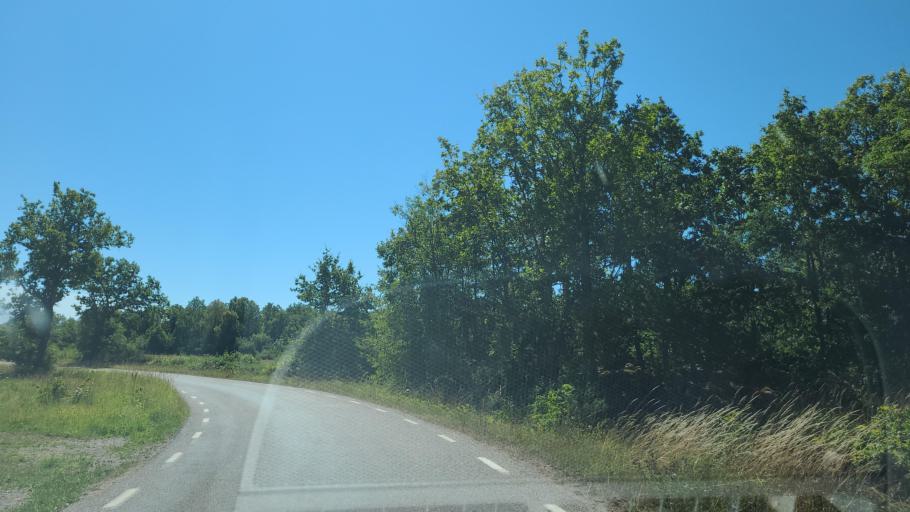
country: SE
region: Kalmar
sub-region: Borgholms Kommun
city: Borgholm
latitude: 56.7469
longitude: 16.6599
